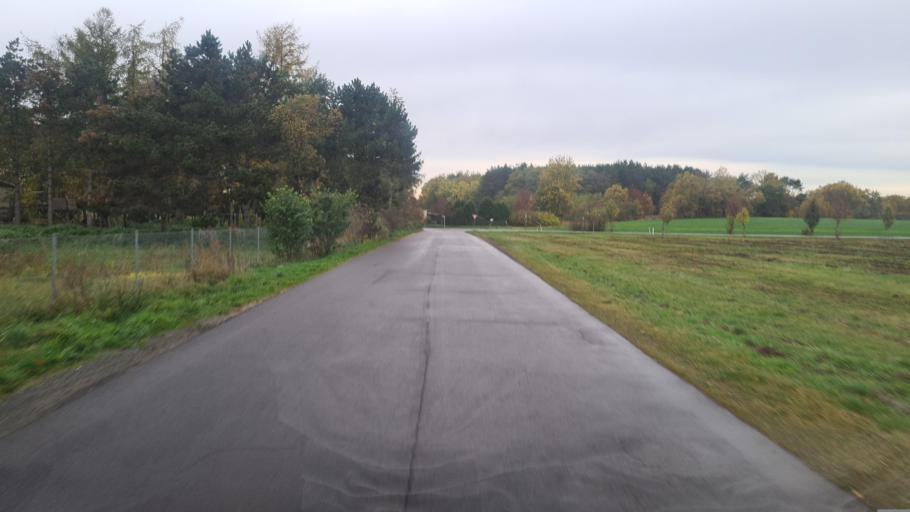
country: DE
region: Saxony-Anhalt
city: Abtsdorf
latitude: 51.9166
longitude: 12.6957
